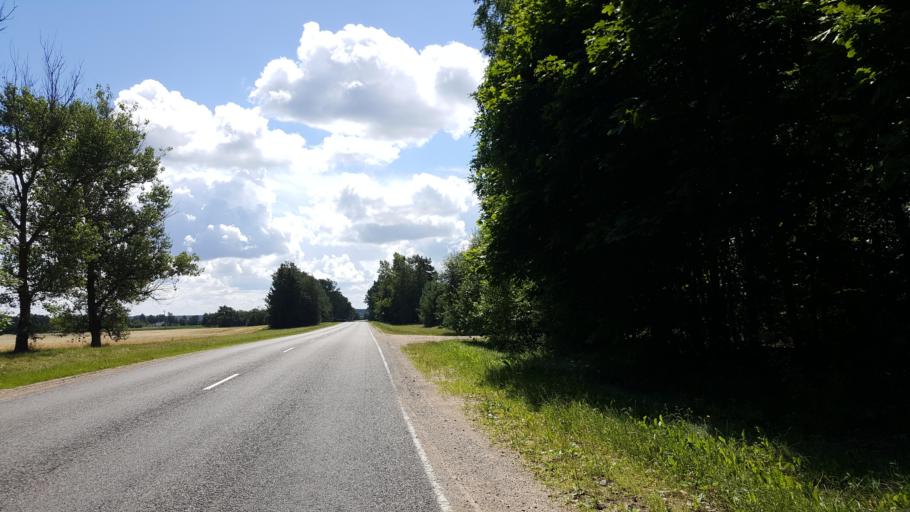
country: BY
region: Brest
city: Kamyanyets
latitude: 52.3765
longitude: 23.8720
